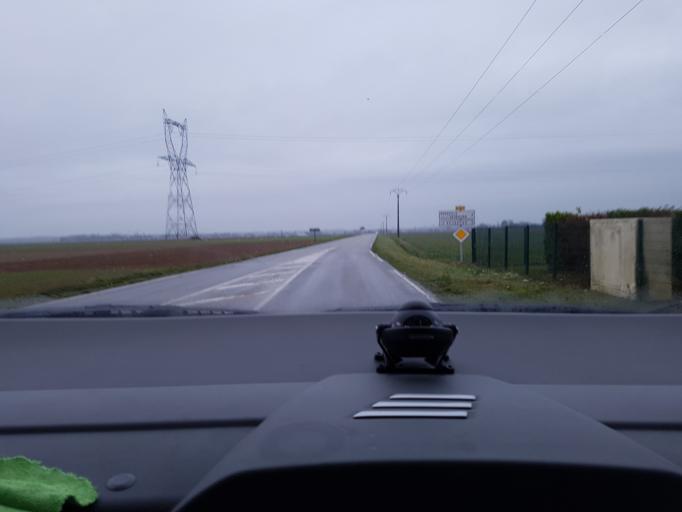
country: FR
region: Haute-Normandie
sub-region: Departement de l'Eure
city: Le Neubourg
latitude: 49.1222
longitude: 0.8643
